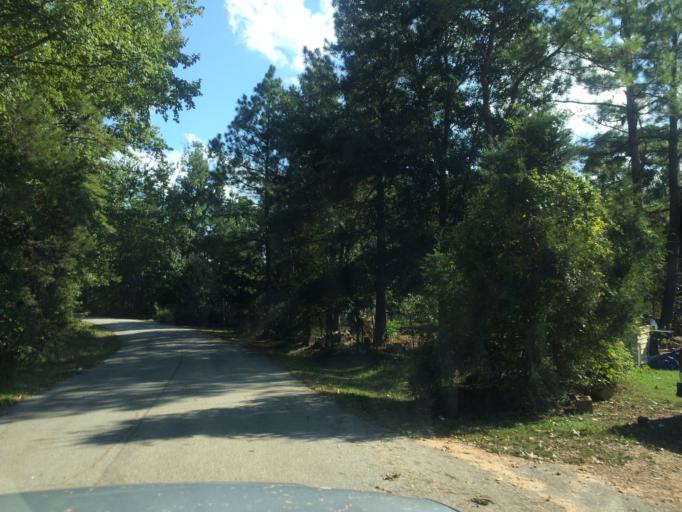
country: US
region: South Carolina
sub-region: Greenwood County
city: Ware Shoals
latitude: 34.4620
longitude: -82.1770
